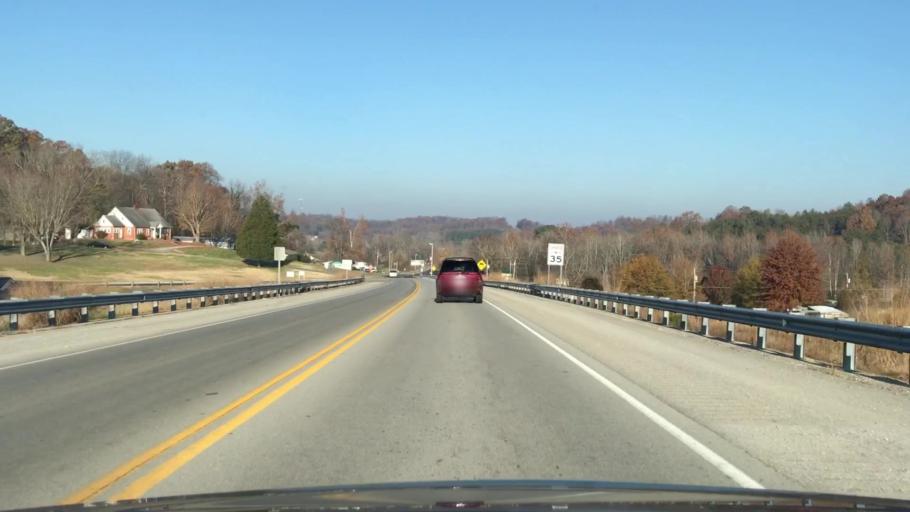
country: US
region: Kentucky
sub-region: Edmonson County
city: Brownsville
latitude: 37.1840
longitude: -86.2480
